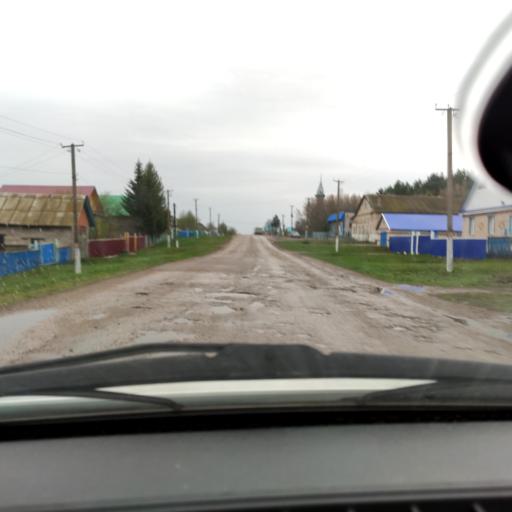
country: RU
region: Bashkortostan
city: Tolbazy
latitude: 54.1710
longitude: 55.9572
